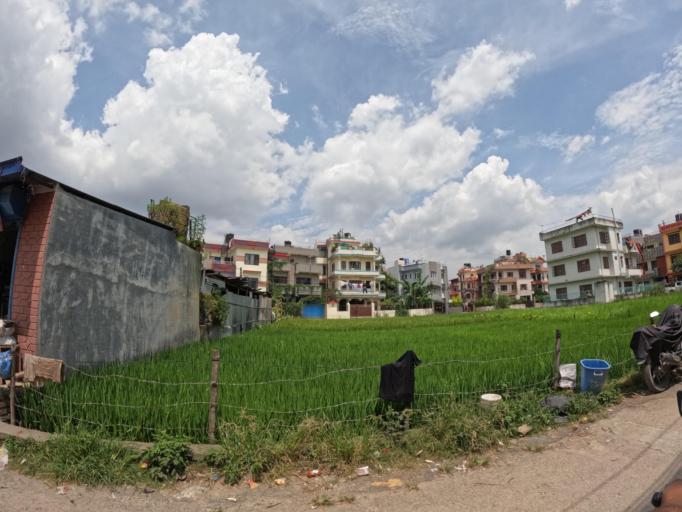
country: NP
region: Central Region
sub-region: Bagmati Zone
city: Kathmandu
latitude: 27.6784
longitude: 85.3694
